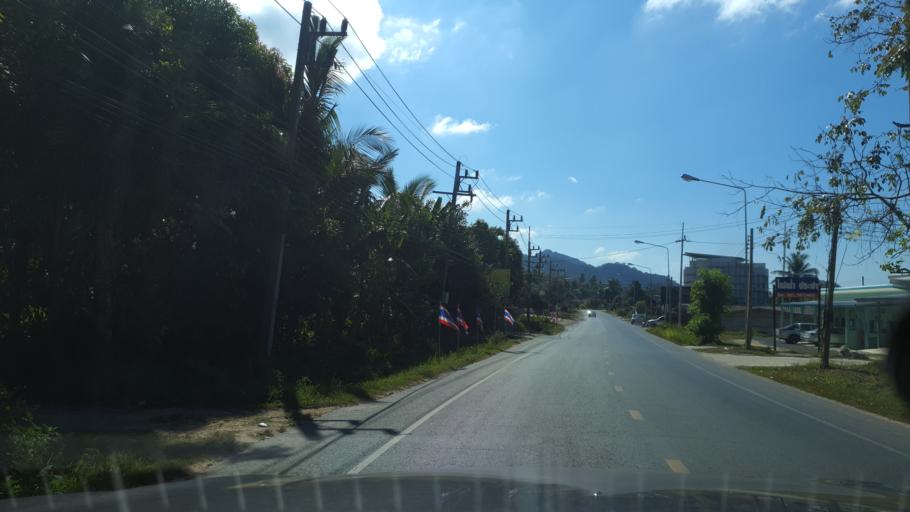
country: TH
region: Phangnga
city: Ban Ao Nang
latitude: 8.0608
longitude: 98.8134
